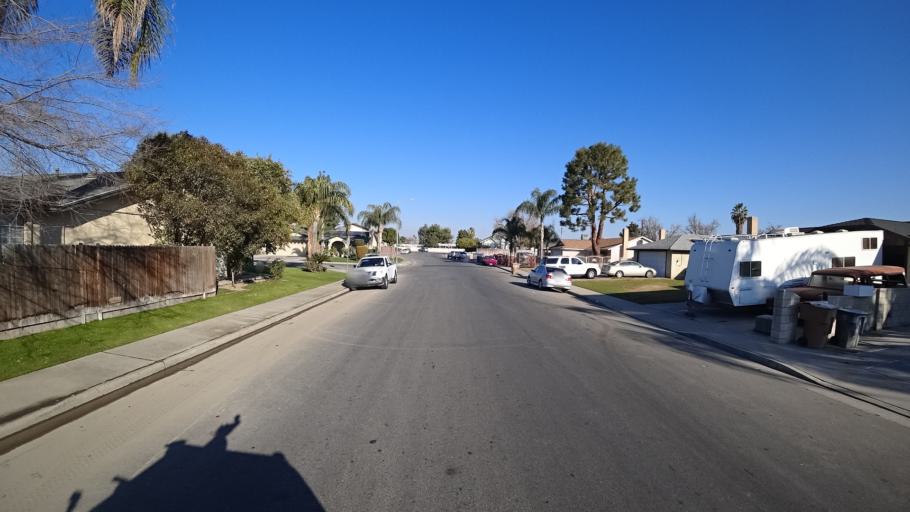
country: US
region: California
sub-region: Kern County
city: Greenfield
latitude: 35.3092
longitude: -119.0193
